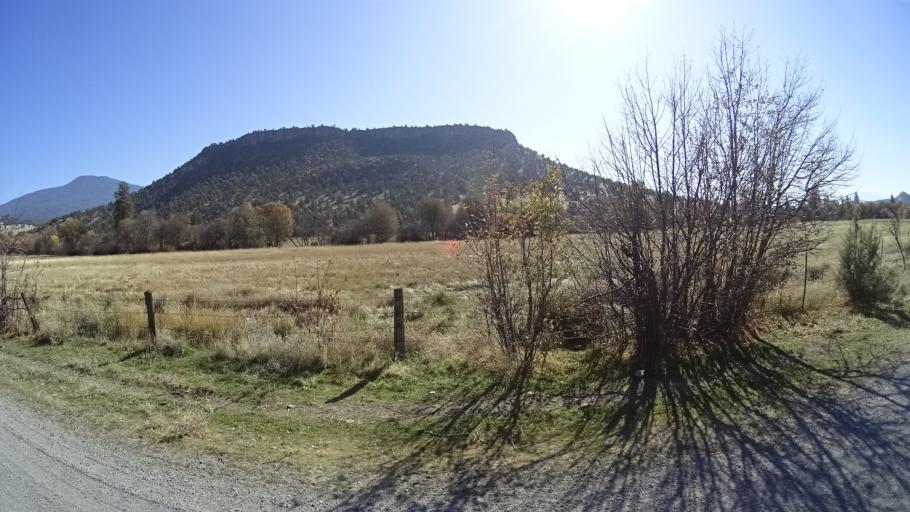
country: US
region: California
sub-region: Siskiyou County
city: Montague
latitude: 41.7379
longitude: -122.3447
